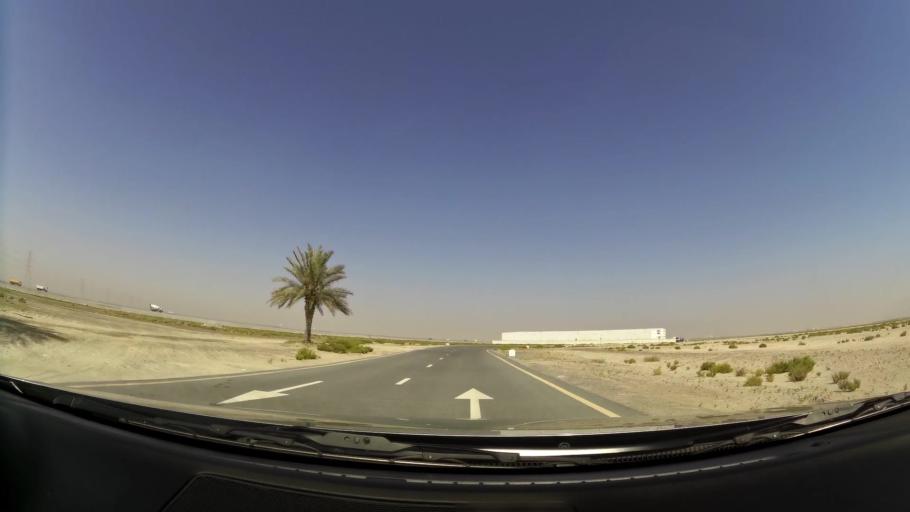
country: AE
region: Dubai
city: Dubai
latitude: 24.8976
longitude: 55.0575
